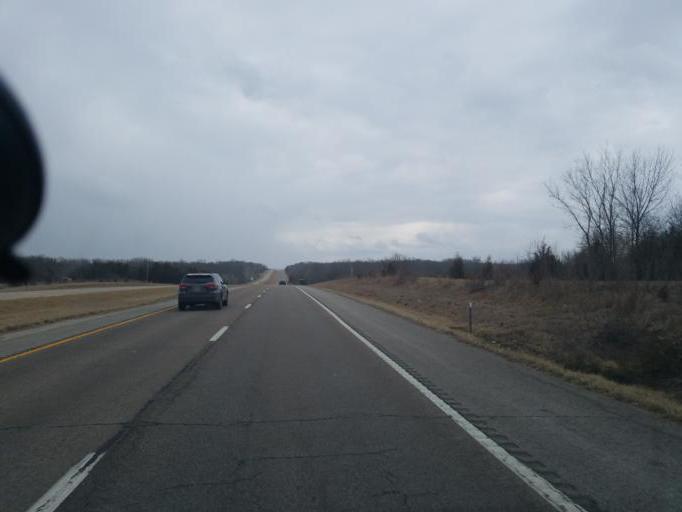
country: US
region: Missouri
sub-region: Boone County
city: Hallsville
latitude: 39.1088
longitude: -92.3292
